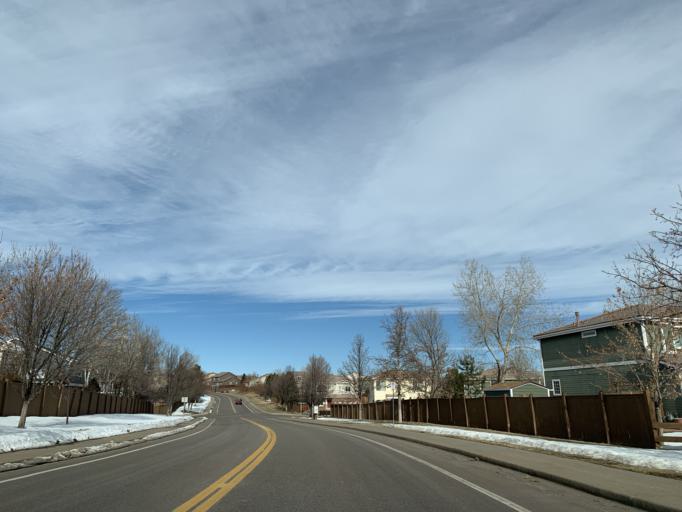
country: US
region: Colorado
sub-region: Douglas County
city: Carriage Club
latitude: 39.5301
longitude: -104.9336
